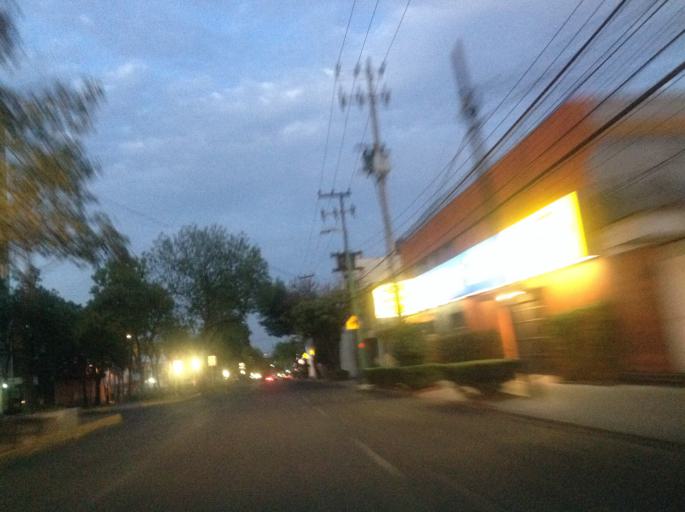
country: MX
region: Mexico City
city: Miguel Hidalgo
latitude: 19.4428
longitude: -99.2145
